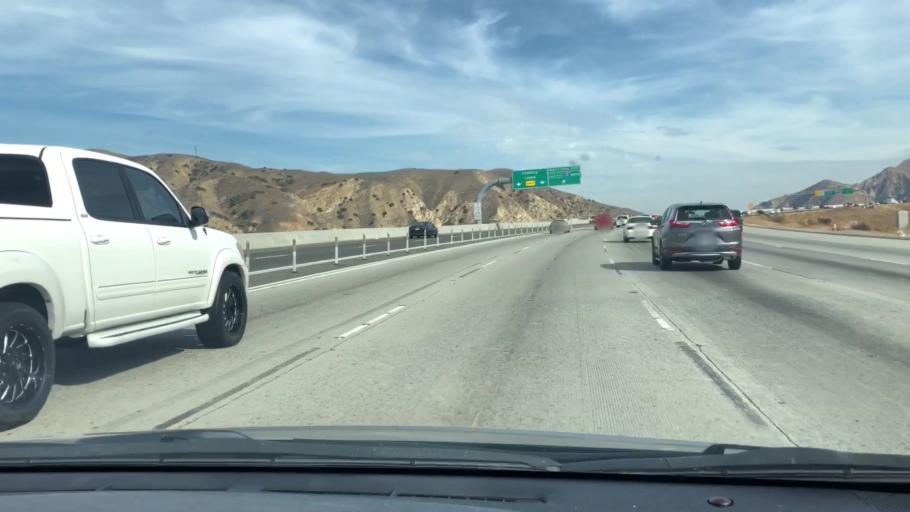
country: US
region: California
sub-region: San Bernardino County
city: Los Serranos
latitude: 33.8735
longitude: -117.6961
